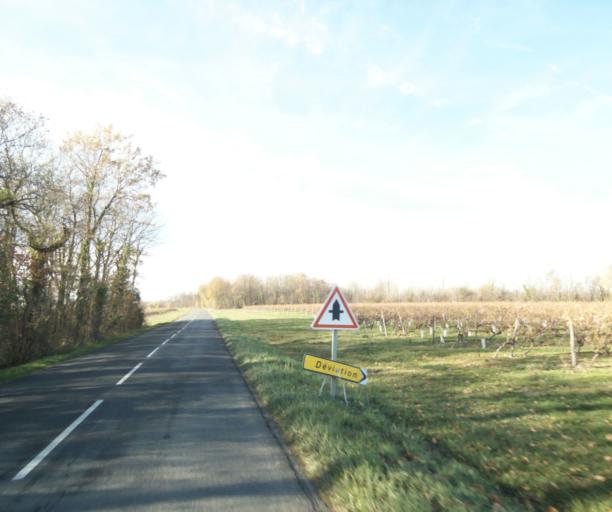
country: FR
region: Poitou-Charentes
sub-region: Departement de la Charente-Maritime
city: Burie
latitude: 45.7691
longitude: -0.4441
